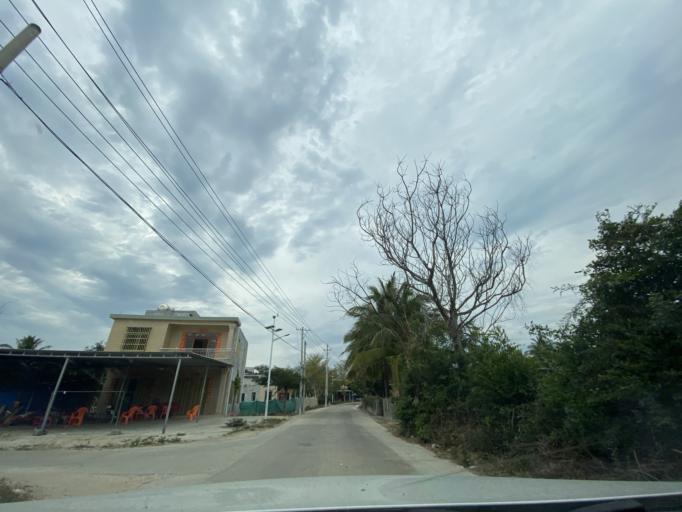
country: CN
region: Hainan
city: Yingzhou
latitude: 18.4157
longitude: 109.8226
